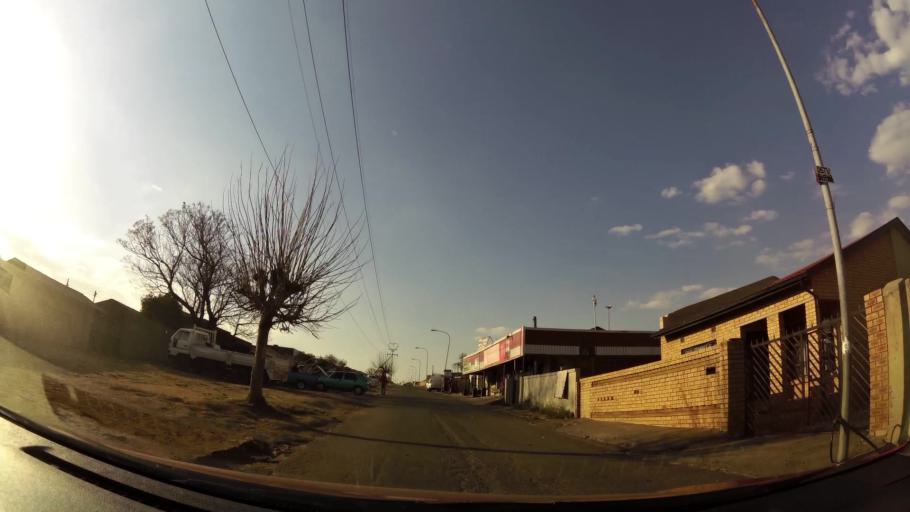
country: ZA
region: Gauteng
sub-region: City of Johannesburg Metropolitan Municipality
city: Soweto
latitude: -26.2242
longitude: 27.9065
